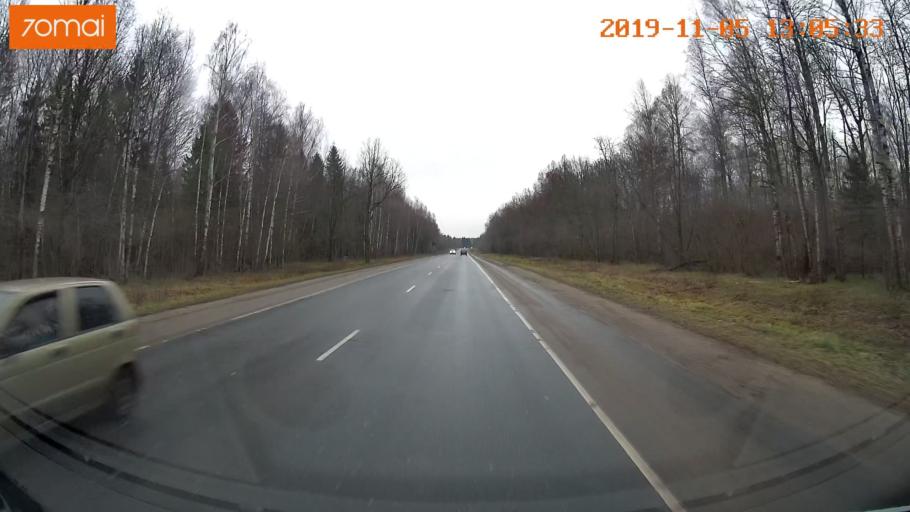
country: RU
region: Ivanovo
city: Kitovo
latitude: 56.8818
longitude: 41.2454
